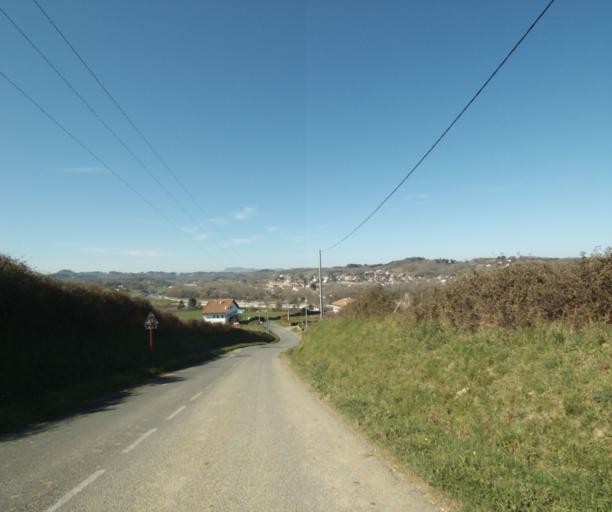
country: FR
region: Aquitaine
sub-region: Departement des Pyrenees-Atlantiques
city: Urrugne
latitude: 43.3624
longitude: -1.6862
